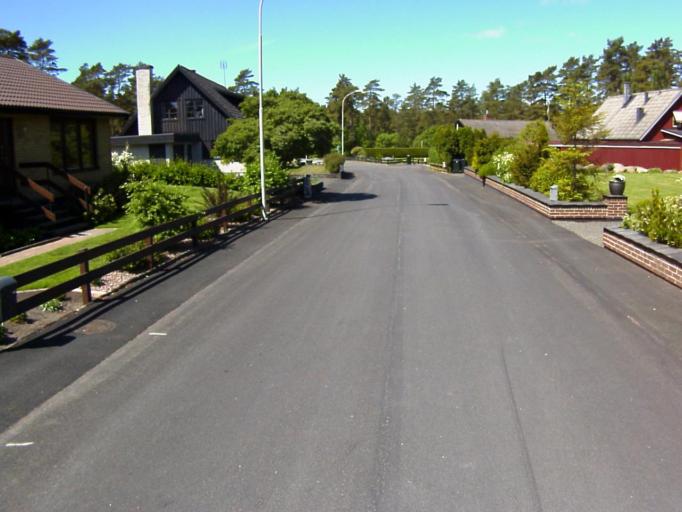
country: SE
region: Skane
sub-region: Kristianstads Kommun
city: Ahus
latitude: 55.9408
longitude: 14.2935
